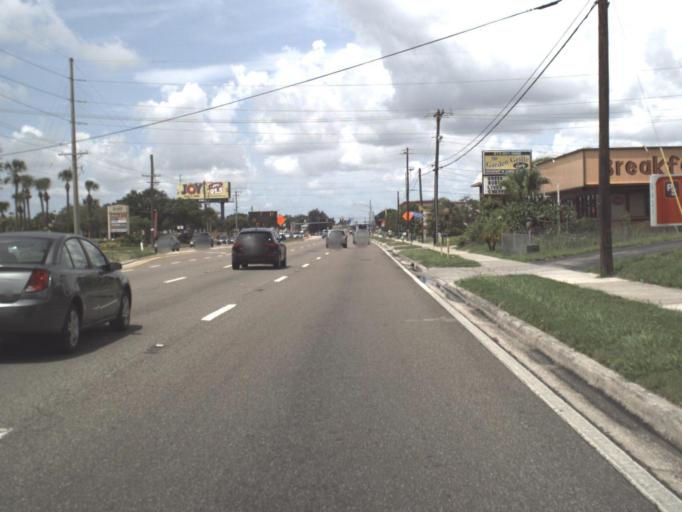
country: US
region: Florida
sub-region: Hillsborough County
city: Town 'n' Country
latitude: 27.9968
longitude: -82.5780
